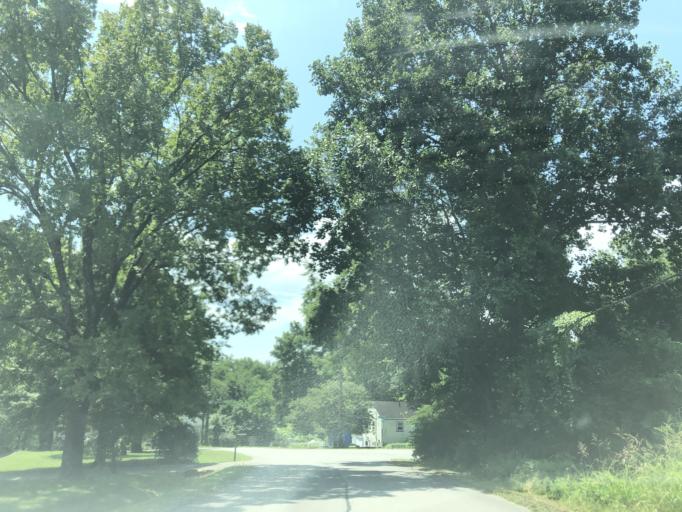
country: US
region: Tennessee
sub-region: Davidson County
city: Lakewood
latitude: 36.1575
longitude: -86.6535
